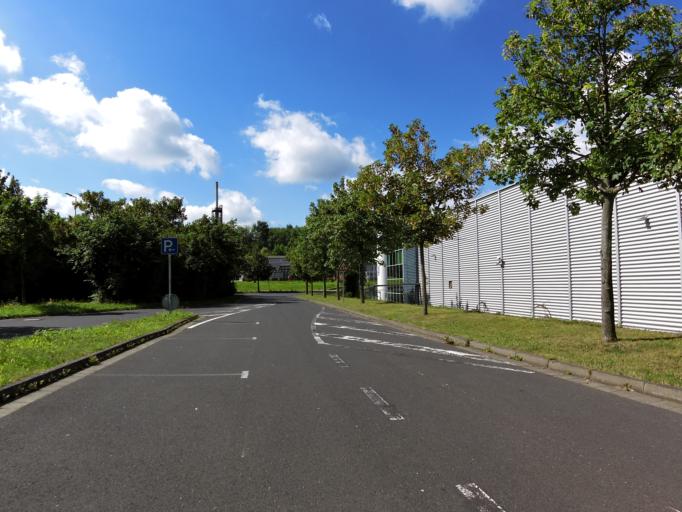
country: DE
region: Thuringia
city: Krauthausen
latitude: 51.0102
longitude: 10.2581
